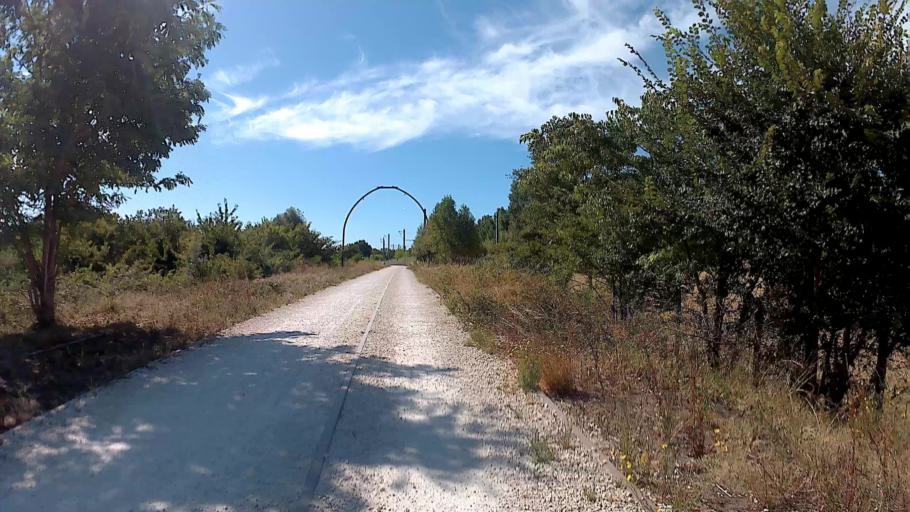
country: FR
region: Aquitaine
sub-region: Departement de la Gironde
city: Le Bouscat
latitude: 44.8708
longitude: -0.5874
